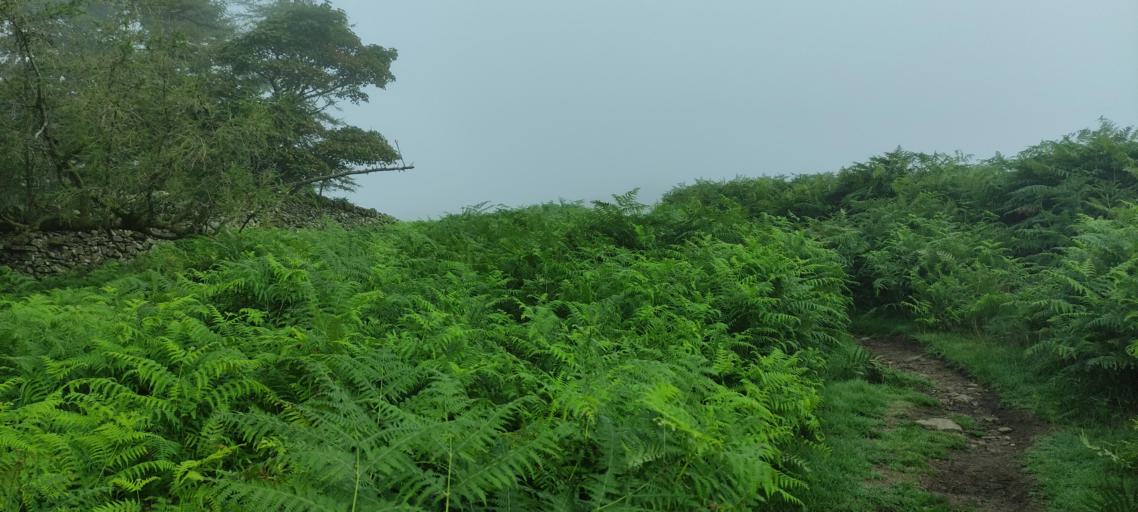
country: GB
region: England
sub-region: Cumbria
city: Ambleside
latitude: 54.4521
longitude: -2.9647
